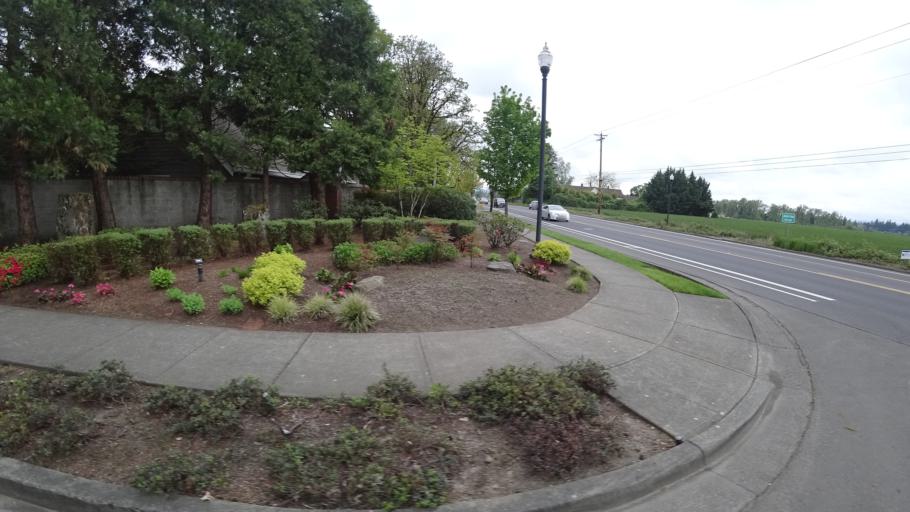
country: US
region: Oregon
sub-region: Washington County
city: Hillsboro
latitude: 45.5499
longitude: -122.9773
